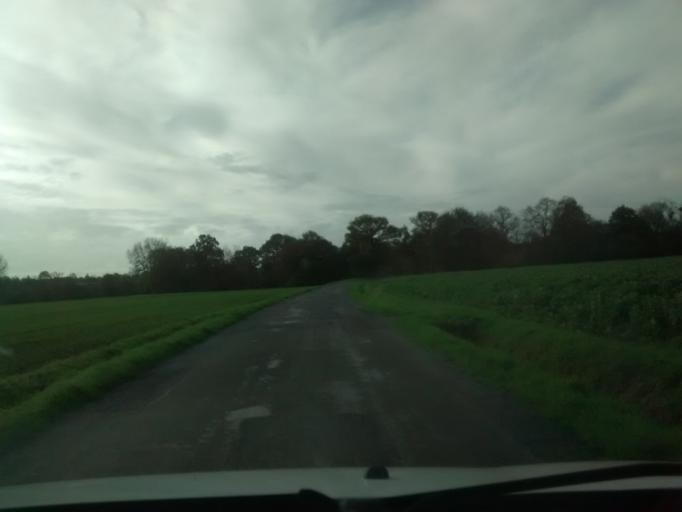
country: FR
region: Brittany
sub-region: Departement d'Ille-et-Vilaine
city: Brece
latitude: 48.1164
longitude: -1.4813
